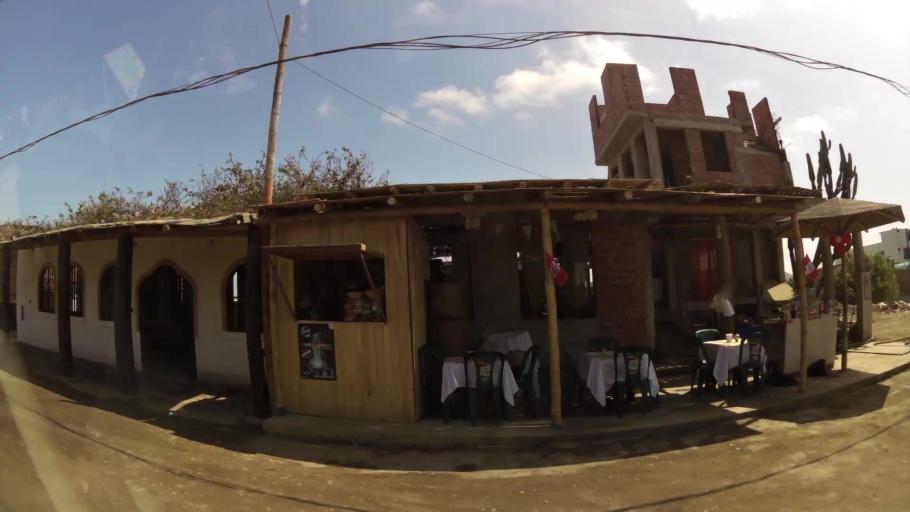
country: PE
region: Lima
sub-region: Provincia de Canete
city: Mala
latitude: -12.6663
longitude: -76.6414
